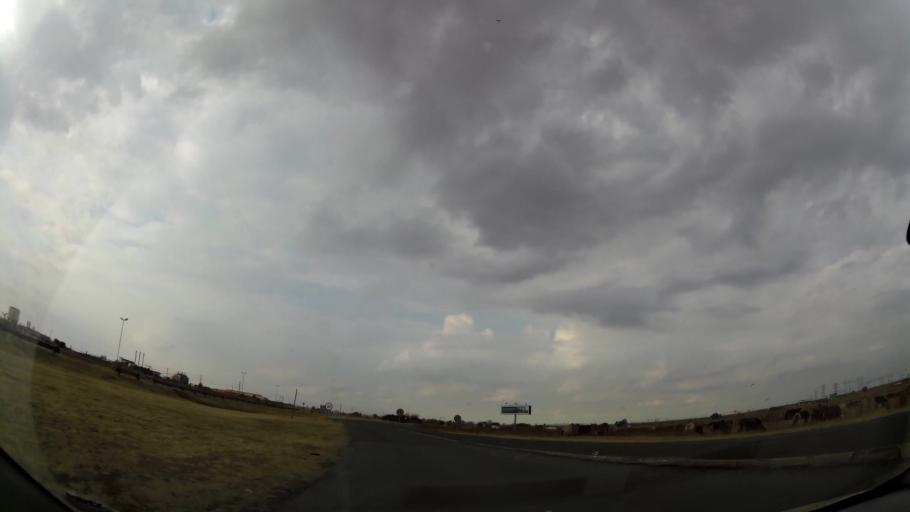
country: ZA
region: Orange Free State
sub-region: Fezile Dabi District Municipality
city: Sasolburg
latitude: -26.8367
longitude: 27.8733
